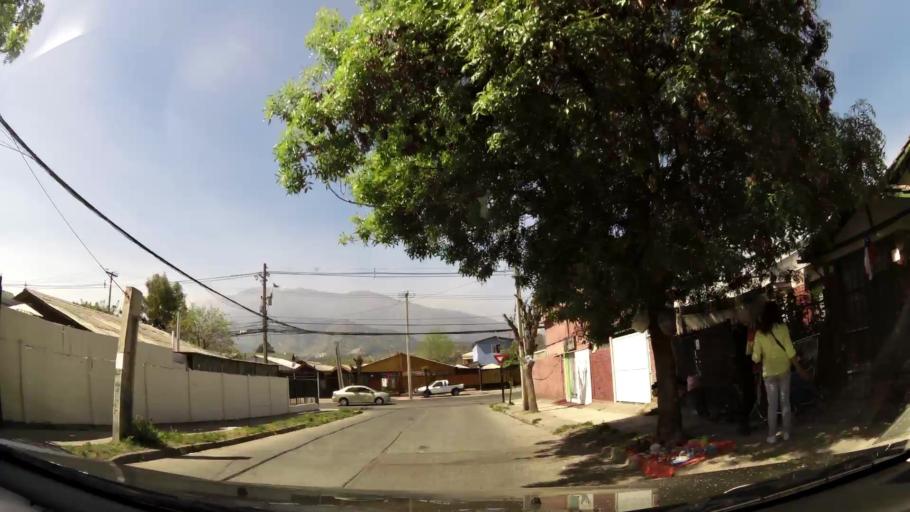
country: CL
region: Santiago Metropolitan
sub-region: Provincia de Cordillera
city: Puente Alto
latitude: -33.5737
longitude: -70.5609
